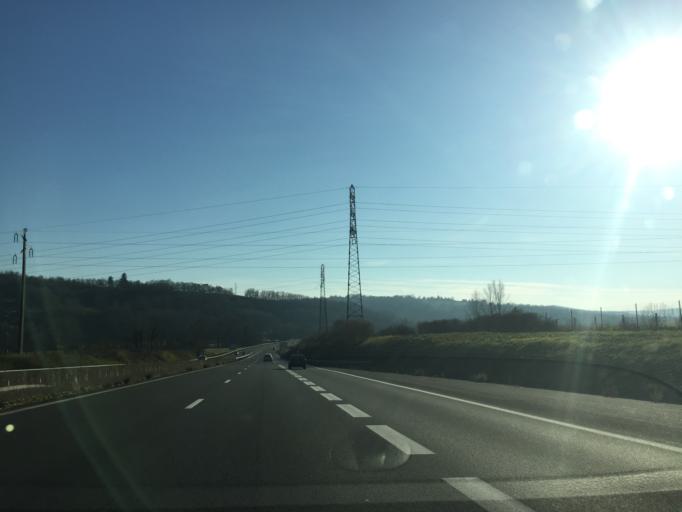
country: FR
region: Limousin
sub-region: Departement de la Correze
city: Donzenac
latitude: 45.2146
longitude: 1.5145
